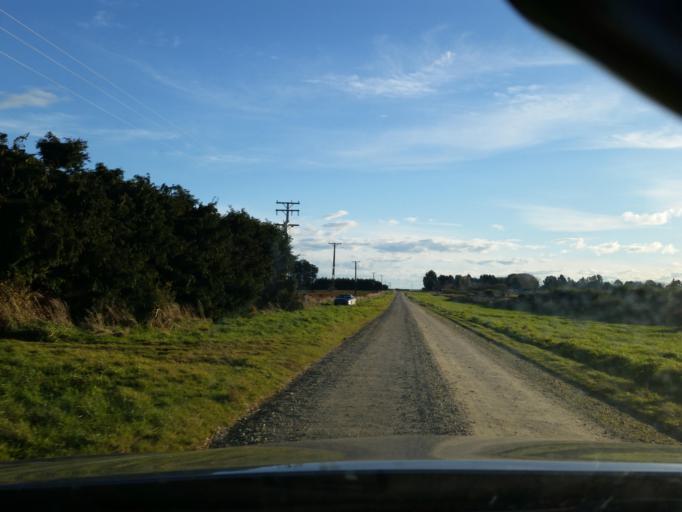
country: NZ
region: Southland
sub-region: Invercargill City
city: Invercargill
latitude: -46.3426
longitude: 168.6321
